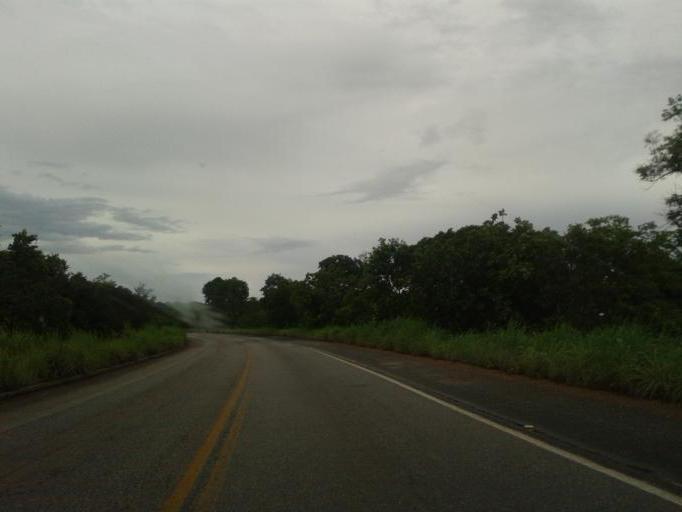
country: BR
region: Goias
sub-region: Mozarlandia
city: Mozarlandia
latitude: -14.8245
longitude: -50.5316
